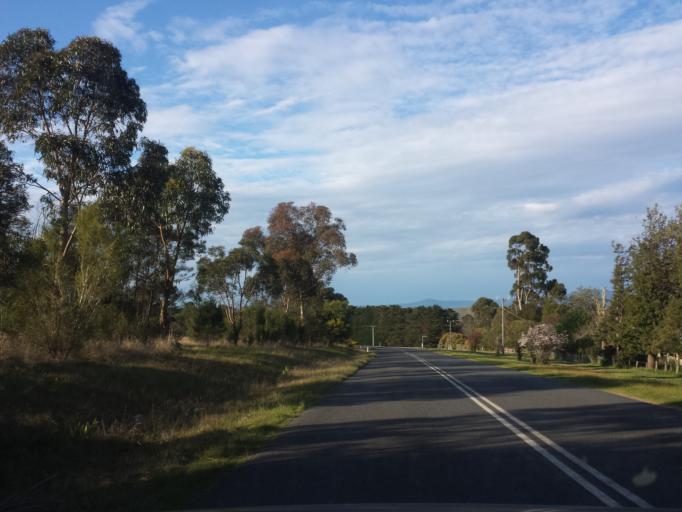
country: AU
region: Victoria
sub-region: Yarra Ranges
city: Yarra Glen
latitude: -37.6426
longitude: 145.3727
